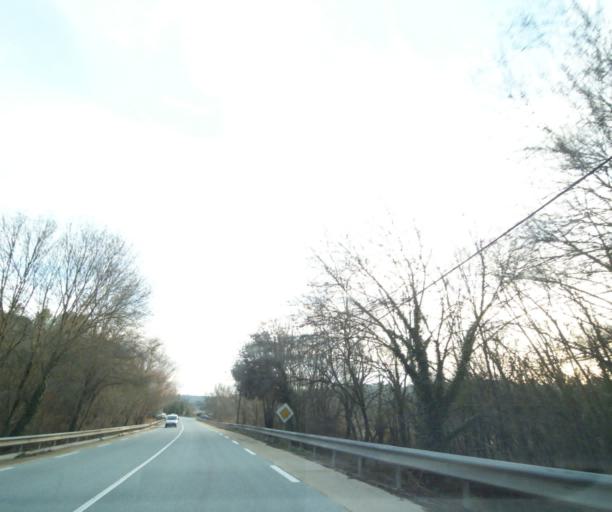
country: FR
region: Provence-Alpes-Cote d'Azur
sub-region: Departement du Var
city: Trans-en-Provence
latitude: 43.4974
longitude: 6.5099
